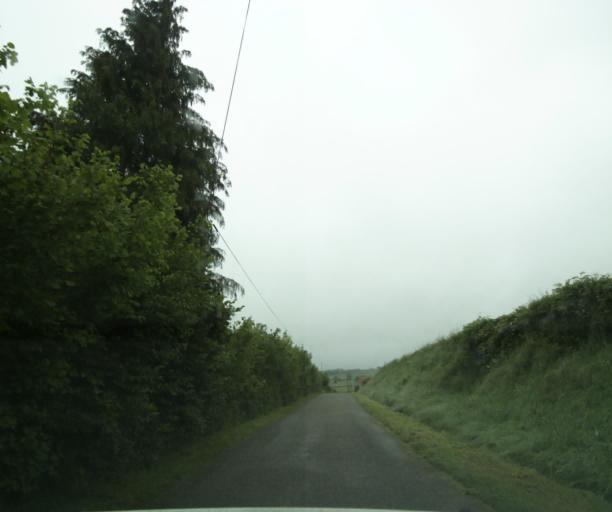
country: FR
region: Bourgogne
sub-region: Departement de Saone-et-Loire
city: Charolles
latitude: 46.3933
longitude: 4.3852
